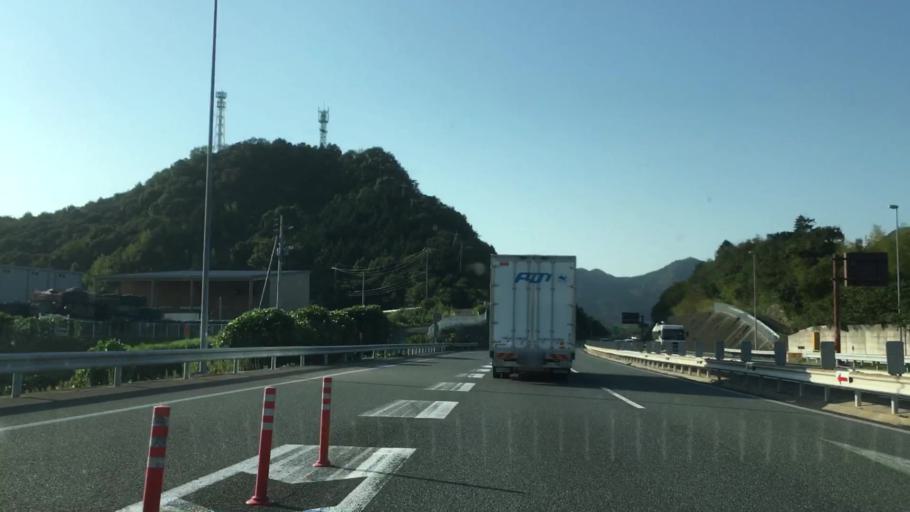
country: JP
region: Yamaguchi
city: Ogori-shimogo
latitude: 34.0887
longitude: 131.4614
